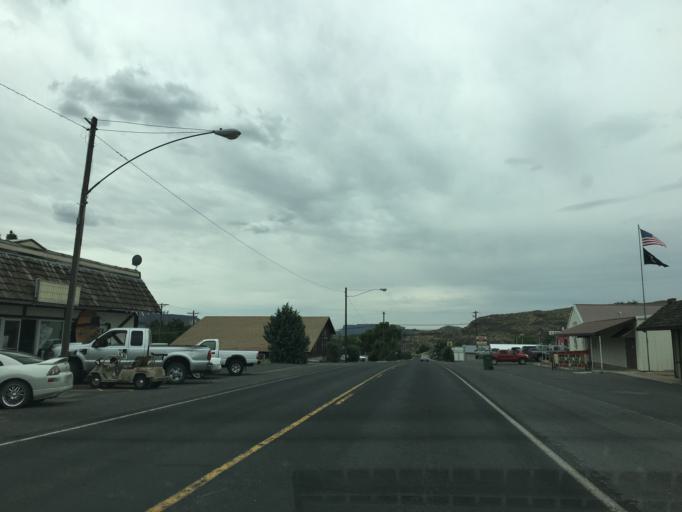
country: US
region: Washington
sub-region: Okanogan County
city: Coulee Dam
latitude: 47.9321
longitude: -119.0390
